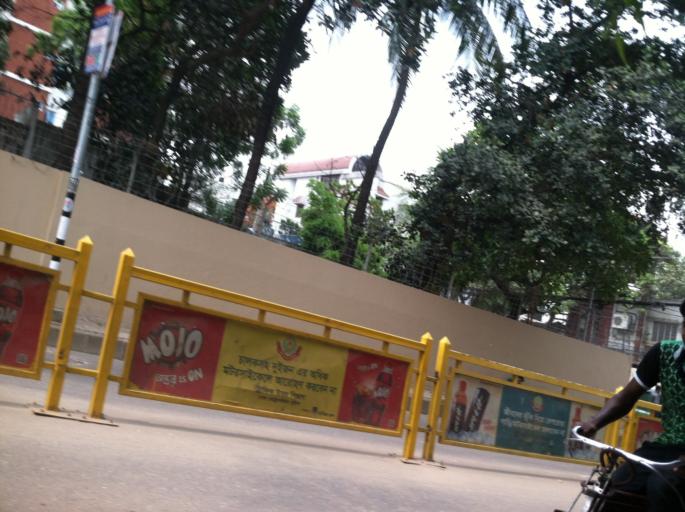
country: BD
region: Dhaka
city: Paltan
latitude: 23.7872
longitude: 90.4034
